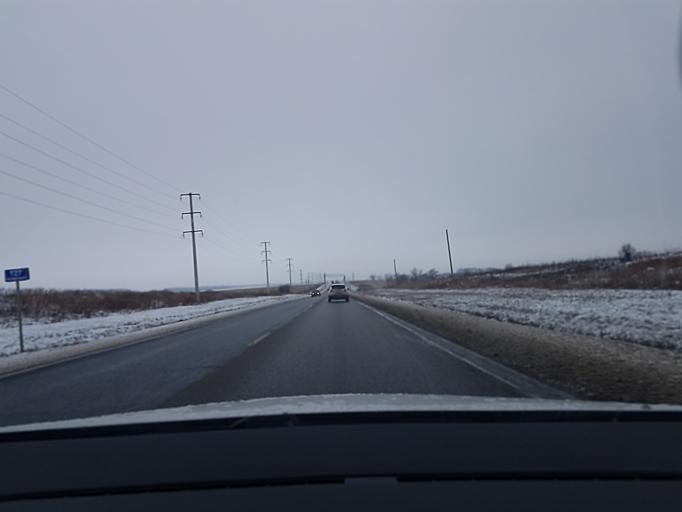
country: RU
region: Moskovskaya
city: Ozherel'ye
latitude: 54.7538
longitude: 38.2162
